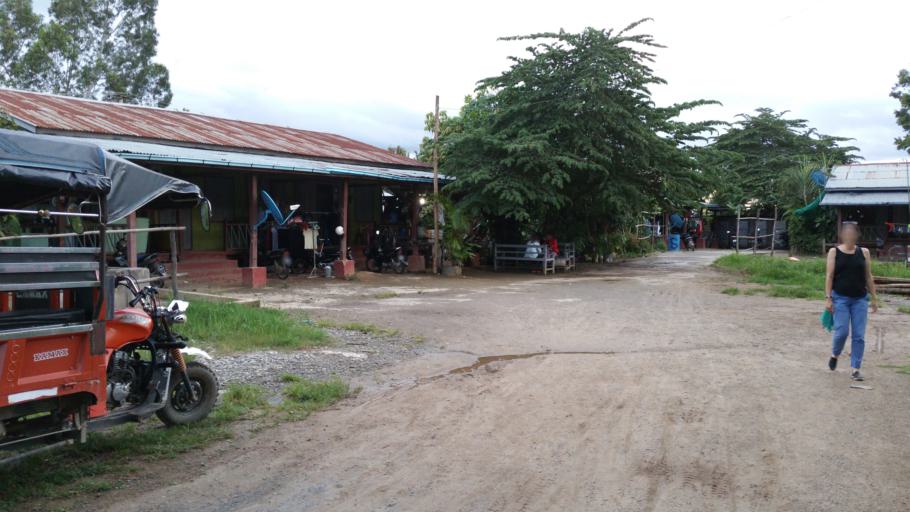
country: MM
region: Shan
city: Taunggyi
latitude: 20.6528
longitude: 96.9241
